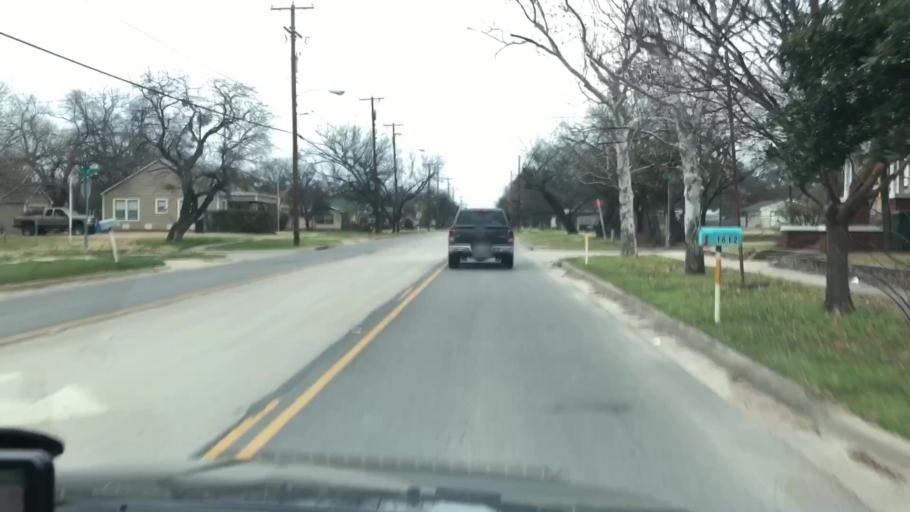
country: US
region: Texas
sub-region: Palo Pinto County
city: Mineral Wells
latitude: 32.8206
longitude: -98.1128
